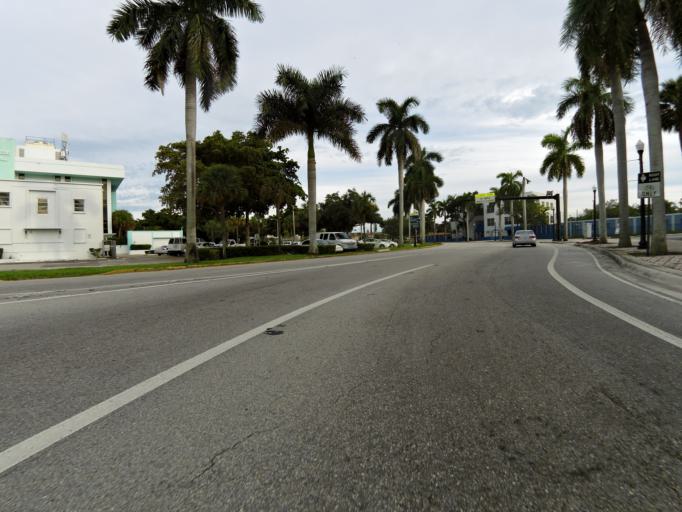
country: US
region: Florida
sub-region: Broward County
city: Hollywood
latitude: 26.0110
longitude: -80.1605
